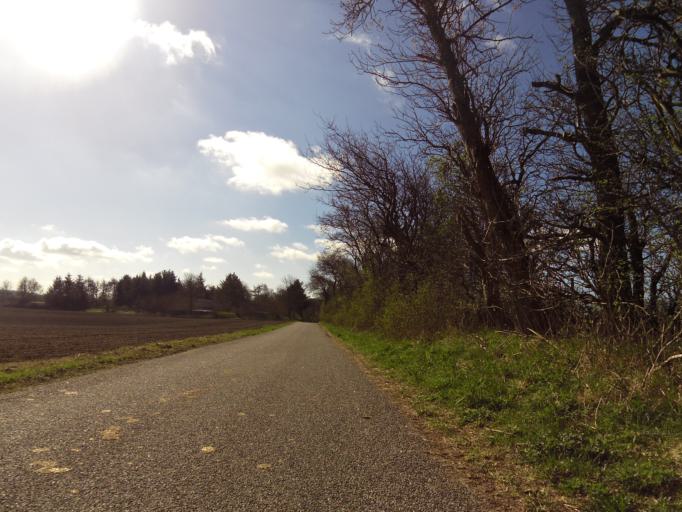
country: DK
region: Central Jutland
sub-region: Holstebro Kommune
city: Vinderup
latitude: 56.4386
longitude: 8.7246
